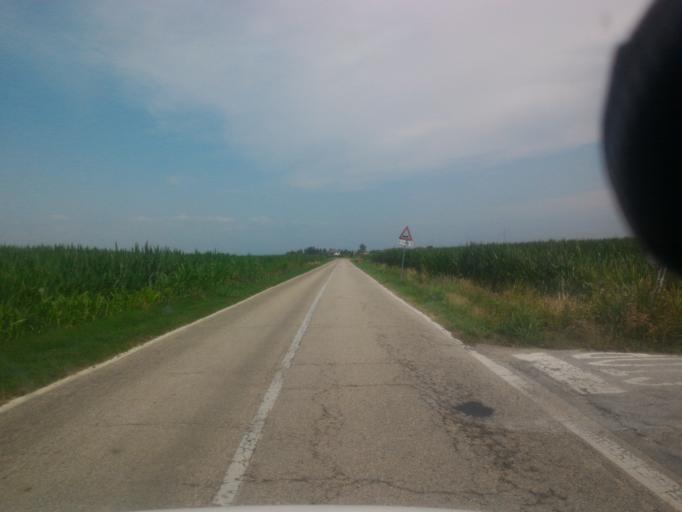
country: IT
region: Piedmont
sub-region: Provincia di Torino
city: Buriasco
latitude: 44.8597
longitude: 7.4276
